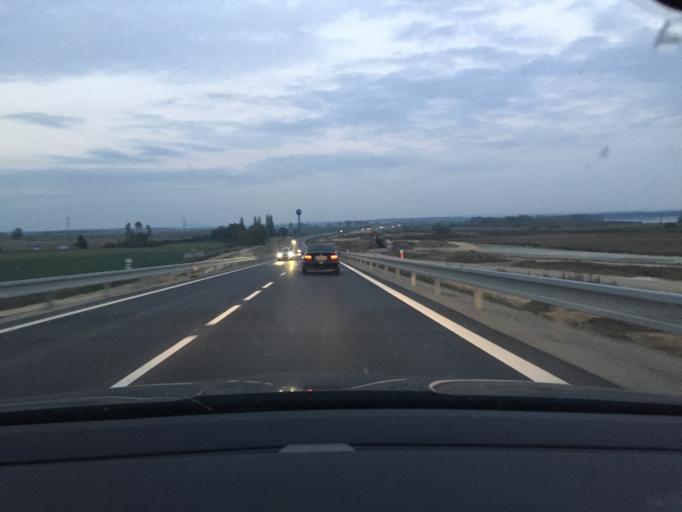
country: CZ
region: Jihocesky
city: Dolni Bukovsko
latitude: 49.1559
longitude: 14.6357
